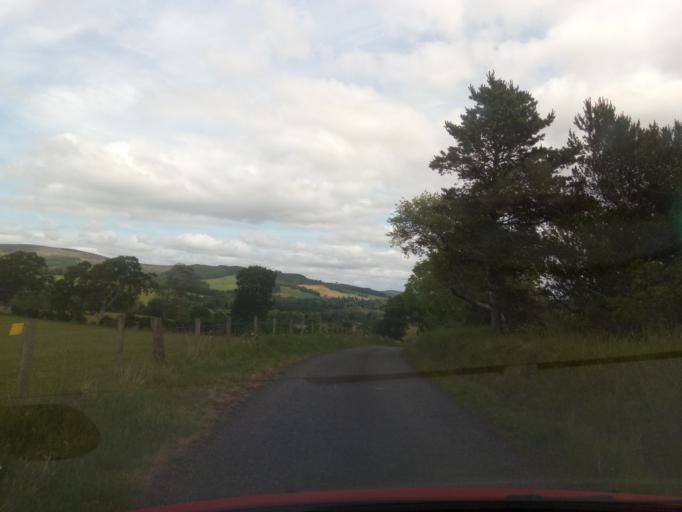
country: GB
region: Scotland
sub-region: The Scottish Borders
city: Selkirk
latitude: 55.5316
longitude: -2.8734
